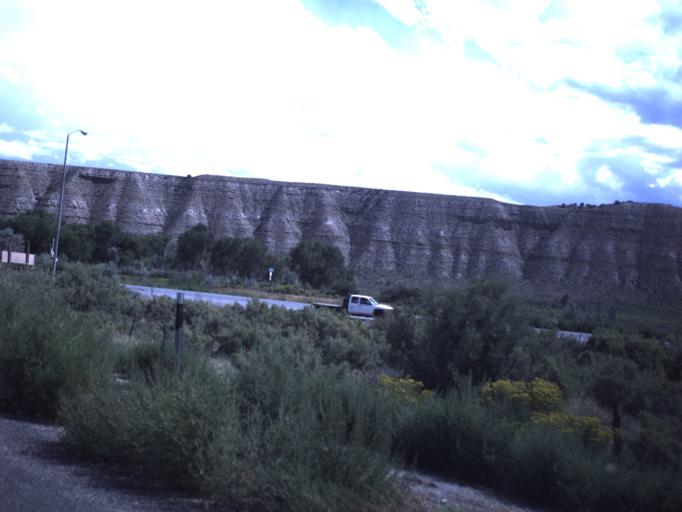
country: US
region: Utah
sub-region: Duchesne County
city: Duchesne
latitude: 40.1642
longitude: -110.4135
